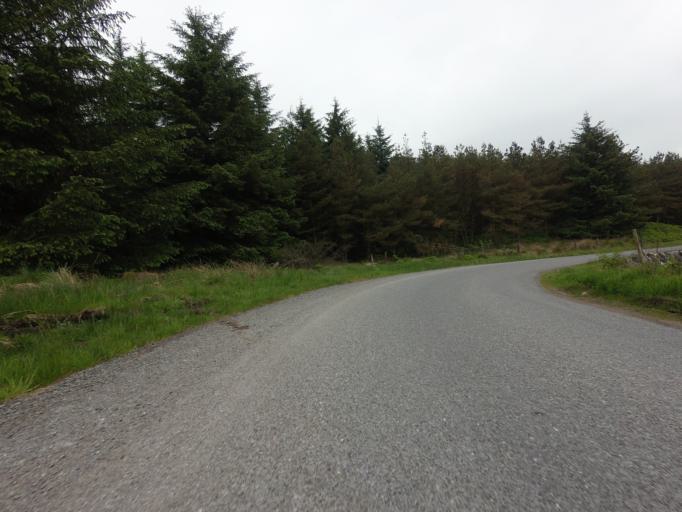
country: GB
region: Scotland
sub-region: Perth and Kinross
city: Kinross
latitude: 56.1573
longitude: -3.4628
